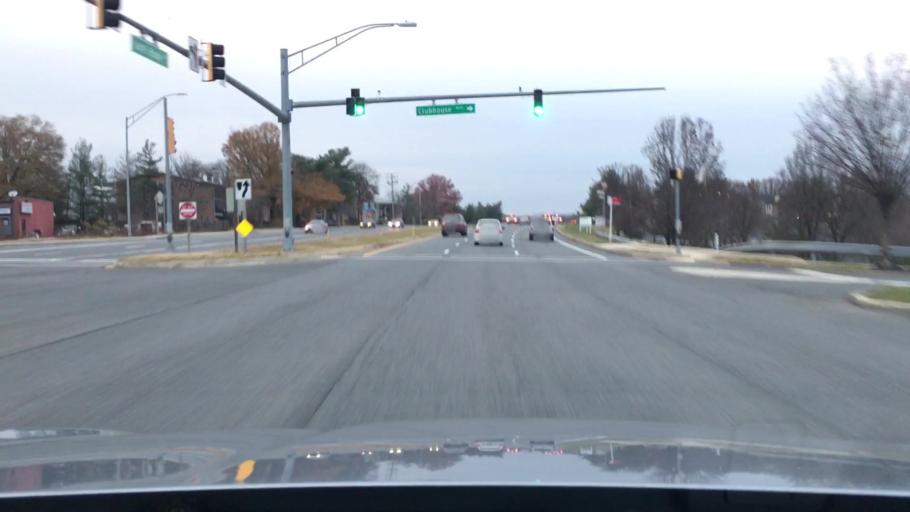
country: US
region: Maryland
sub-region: Prince George's County
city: Laurel
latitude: 39.0888
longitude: -76.8463
